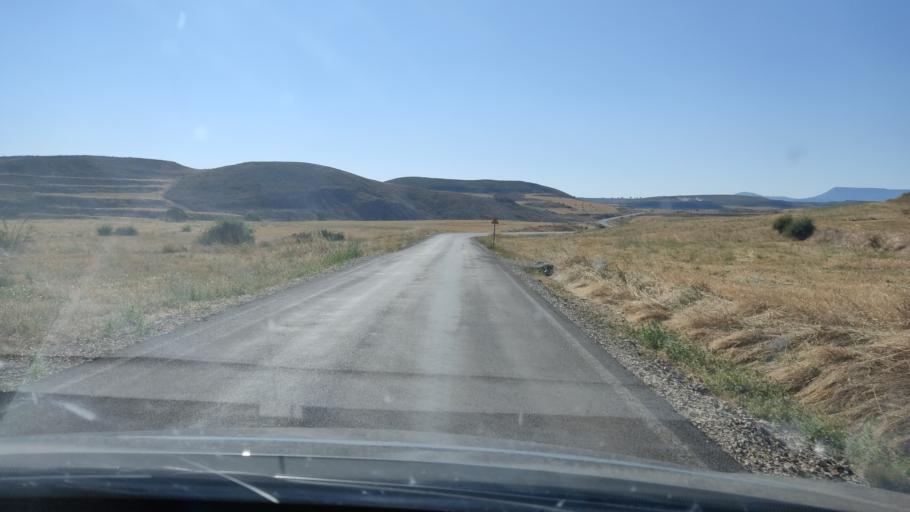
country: ES
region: Aragon
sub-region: Provincia de Teruel
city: Monforte de Moyuela
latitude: 41.0509
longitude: -1.0100
